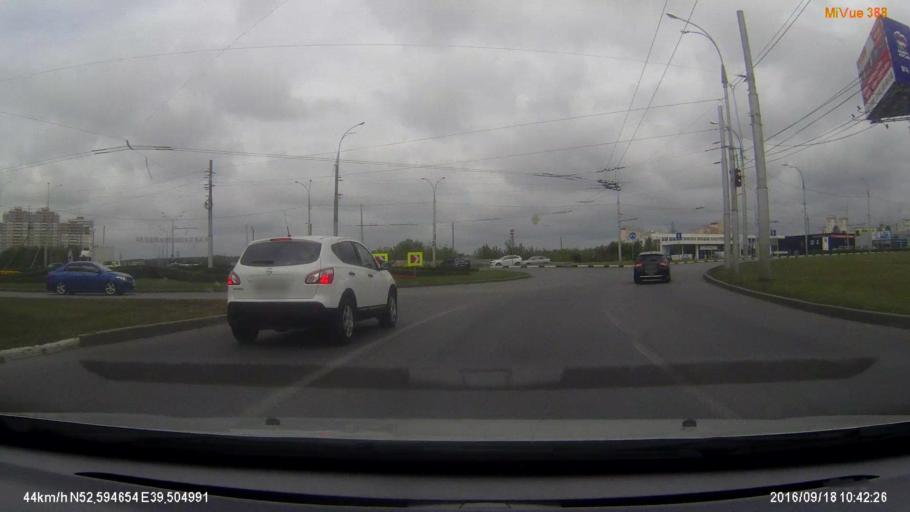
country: RU
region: Lipetsk
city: Syrskoye
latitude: 52.5945
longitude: 39.5051
